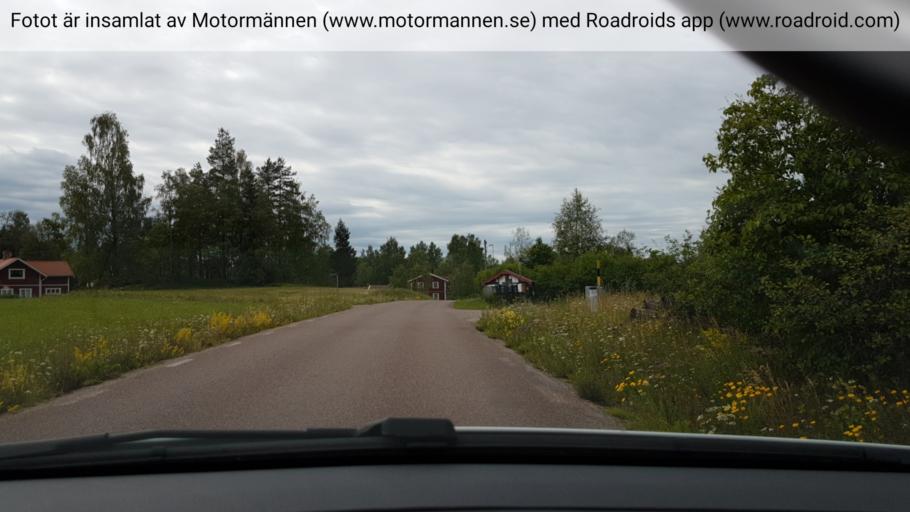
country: SE
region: Dalarna
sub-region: Rattviks Kommun
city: Raettvik
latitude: 60.9188
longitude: 15.1017
